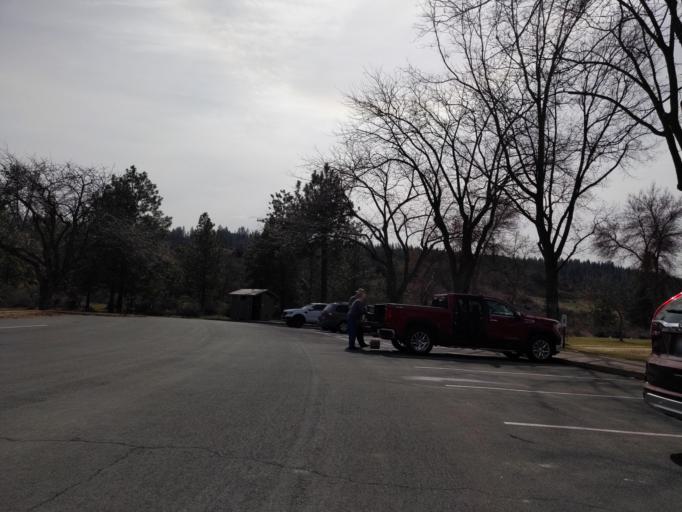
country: US
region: Washington
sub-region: Lincoln County
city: Davenport
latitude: 47.9067
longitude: -118.3144
